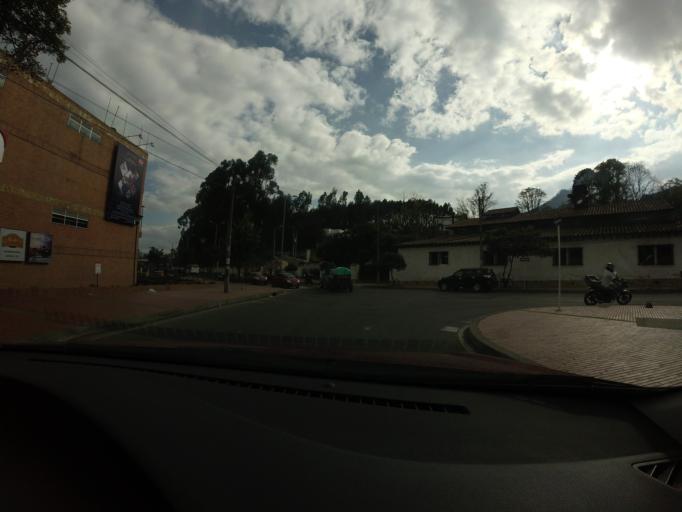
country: CO
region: Cundinamarca
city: Zipaquira
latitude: 5.0187
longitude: -74.0047
